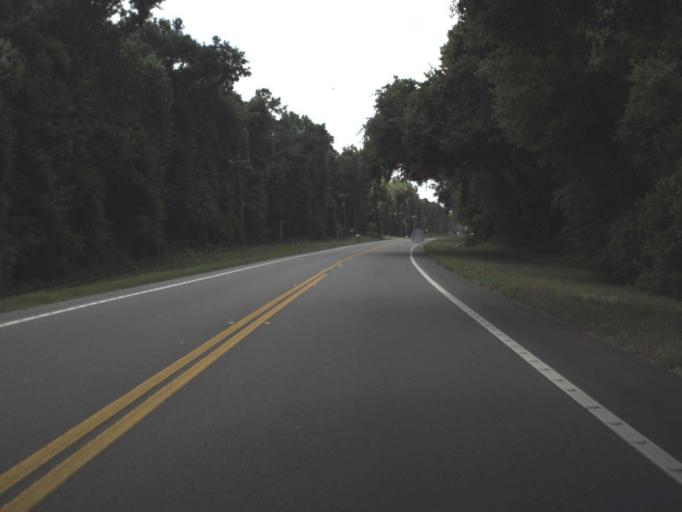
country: US
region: Florida
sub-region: Alachua County
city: Archer
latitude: 29.5398
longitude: -82.4007
